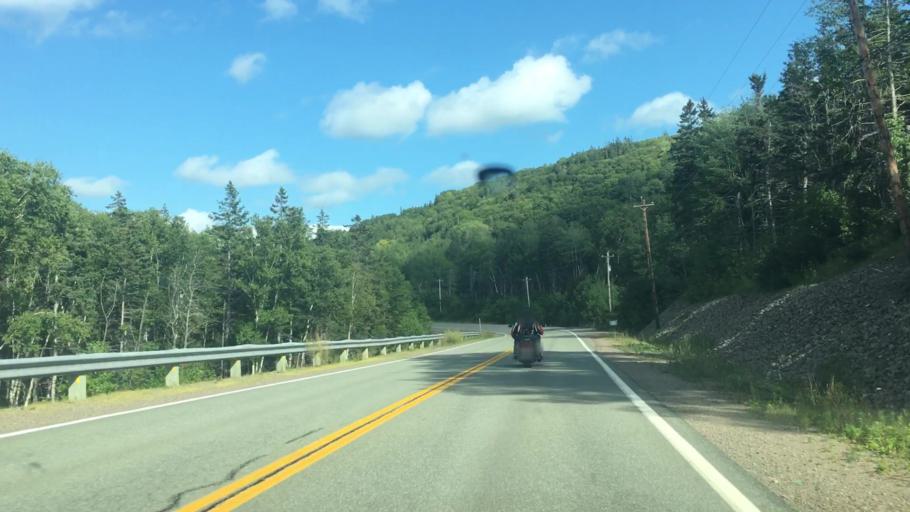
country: CA
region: Nova Scotia
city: Sydney
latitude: 45.8498
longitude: -60.6424
